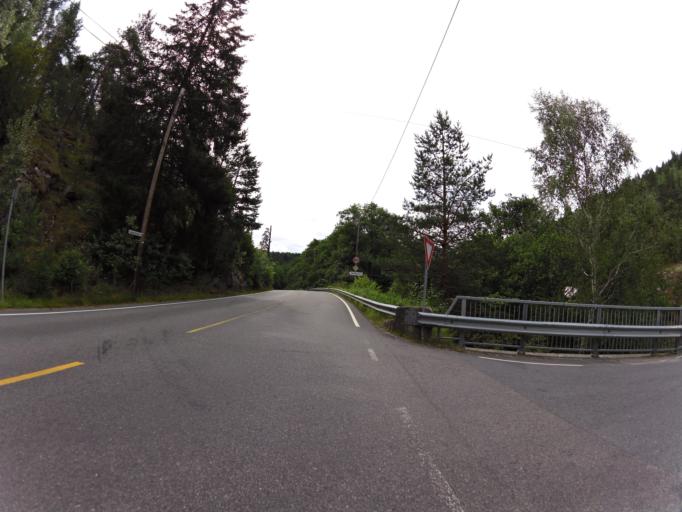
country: NO
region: Akershus
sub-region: Oppegard
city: Kolbotn
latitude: 59.8260
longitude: 10.7700
